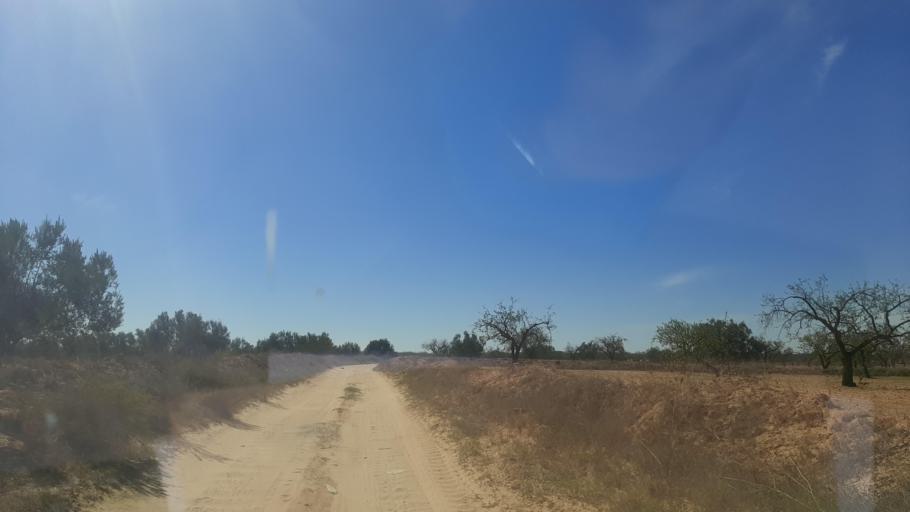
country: TN
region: Safaqis
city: Sfax
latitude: 34.8225
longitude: 10.5526
